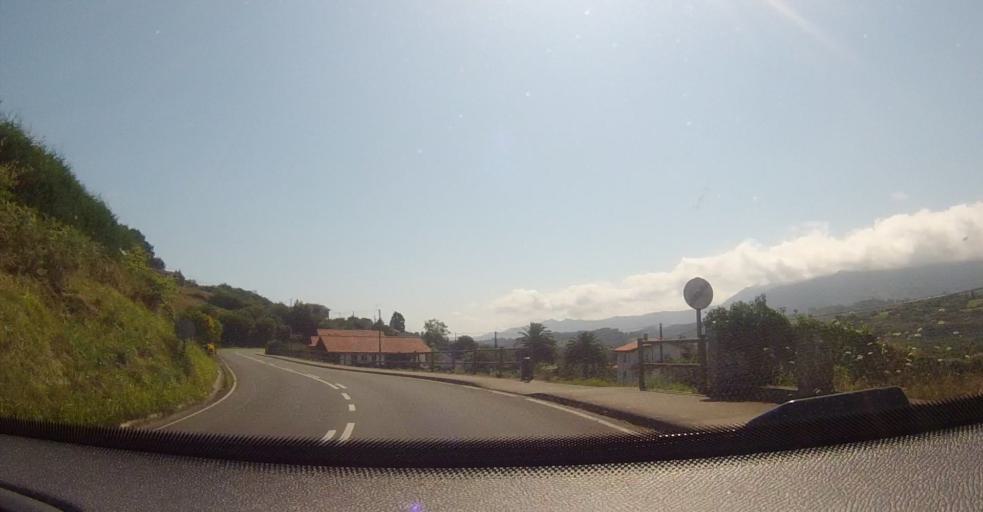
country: ES
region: Asturias
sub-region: Province of Asturias
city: Colunga
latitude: 43.4877
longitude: -5.2937
